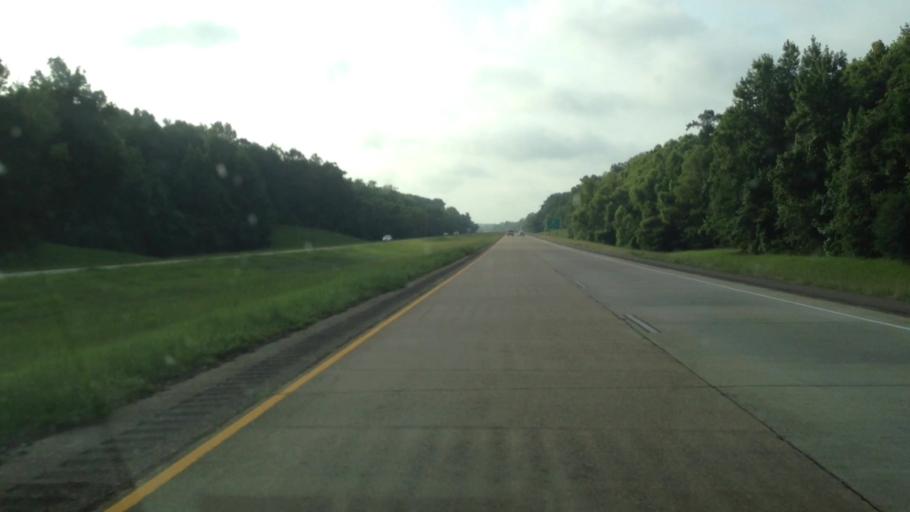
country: US
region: Louisiana
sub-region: Rapides Parish
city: Lecompte
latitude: 31.0248
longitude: -92.3987
